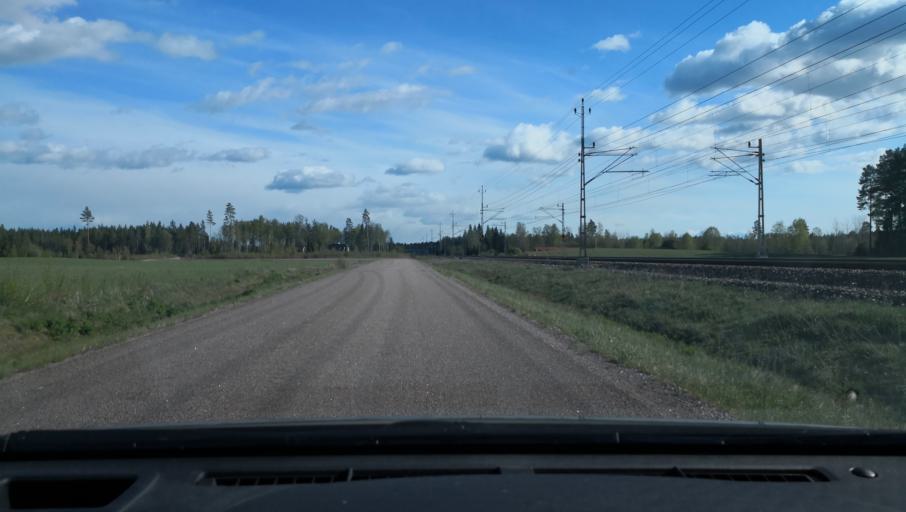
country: SE
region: OErebro
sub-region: Askersunds Kommun
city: Asbro
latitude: 58.9341
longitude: 15.0437
